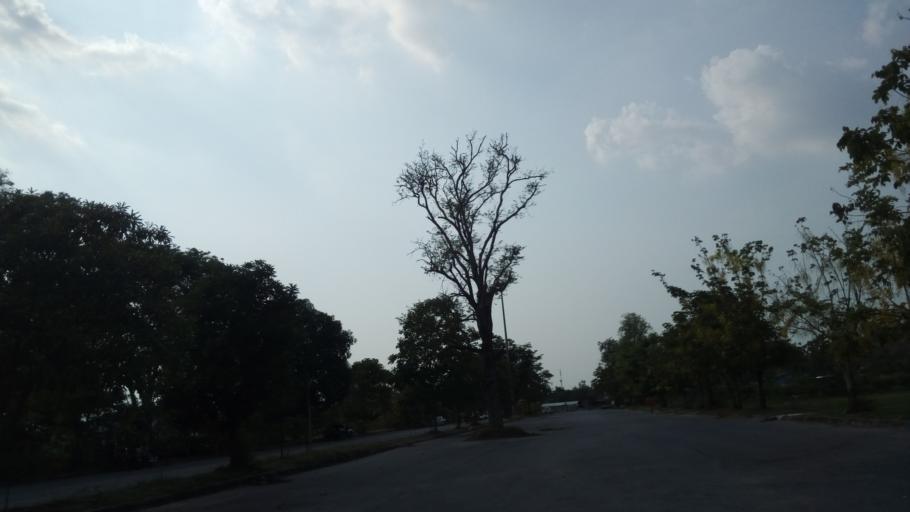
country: TH
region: Sara Buri
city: Saraburi
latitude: 14.4592
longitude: 100.9453
